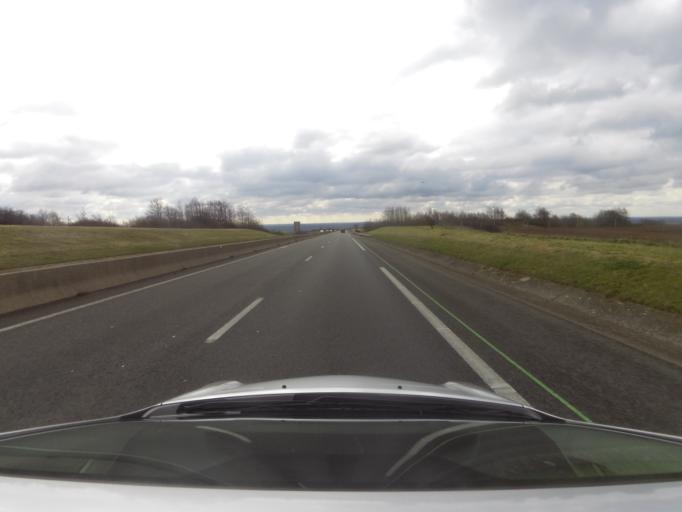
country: FR
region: Nord-Pas-de-Calais
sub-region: Departement du Pas-de-Calais
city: Etaples
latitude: 50.5527
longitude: 1.6713
